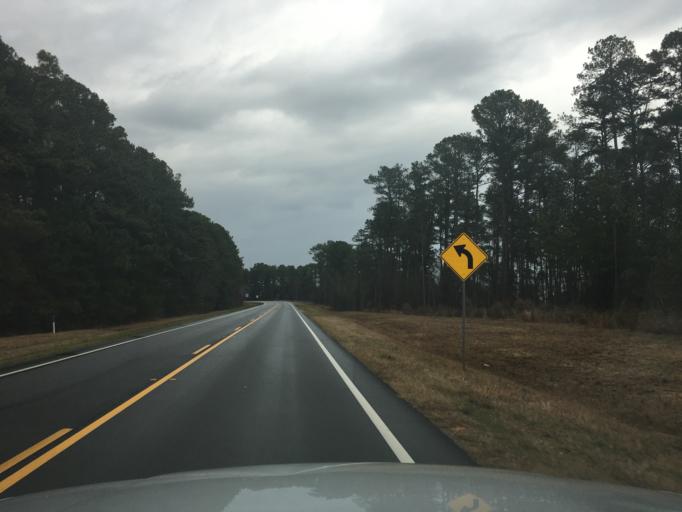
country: US
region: Georgia
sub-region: Columbia County
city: Appling
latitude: 33.6819
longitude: -82.3342
